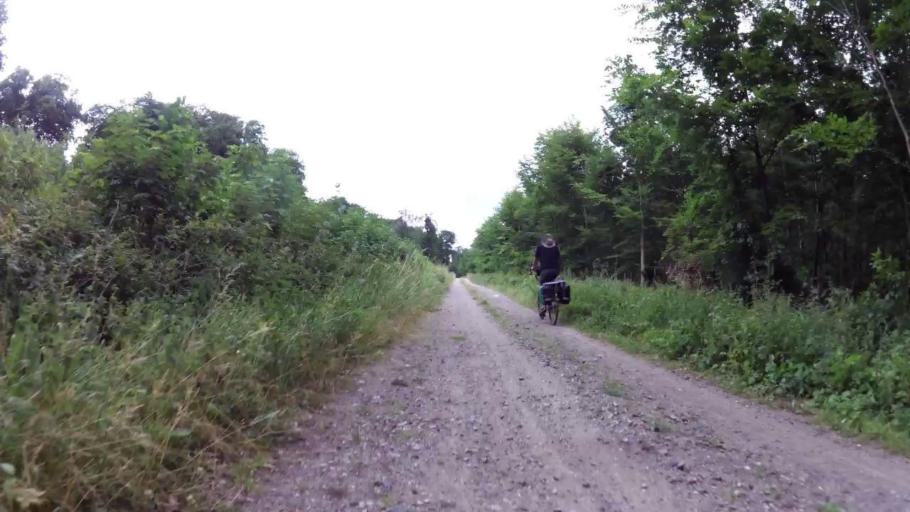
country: PL
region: West Pomeranian Voivodeship
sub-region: Powiat lobeski
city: Lobez
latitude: 53.7582
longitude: 15.5917
